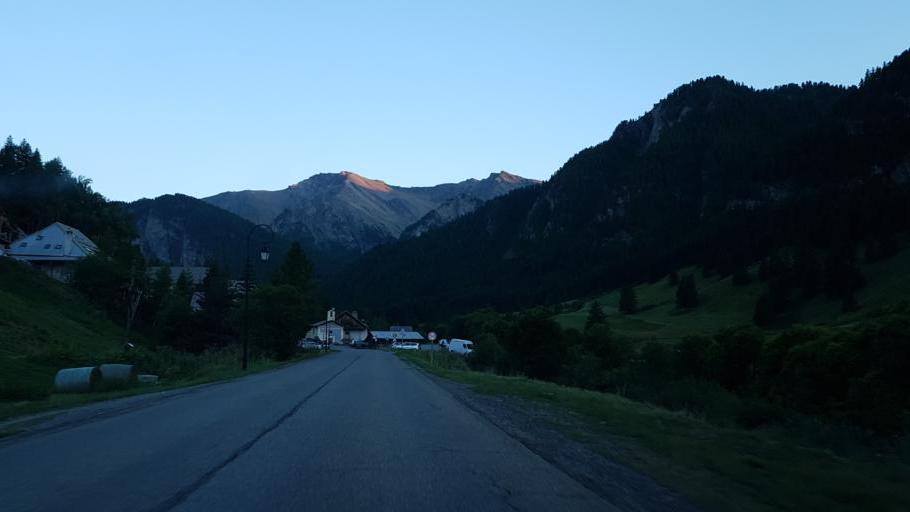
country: IT
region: Piedmont
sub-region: Provincia di Cuneo
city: Pontechianale
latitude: 44.7129
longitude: 6.8486
